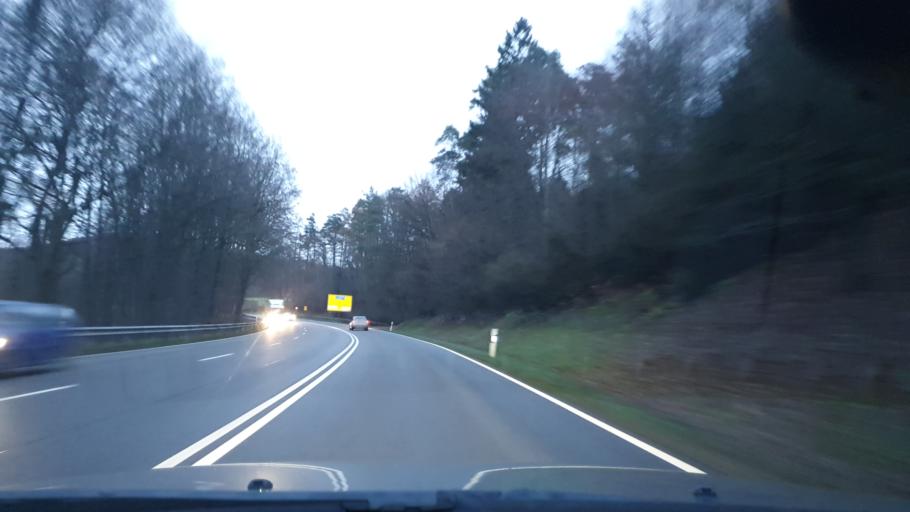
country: DE
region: Rheinland-Pfalz
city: Steinalben
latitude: 49.3234
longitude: 7.6653
